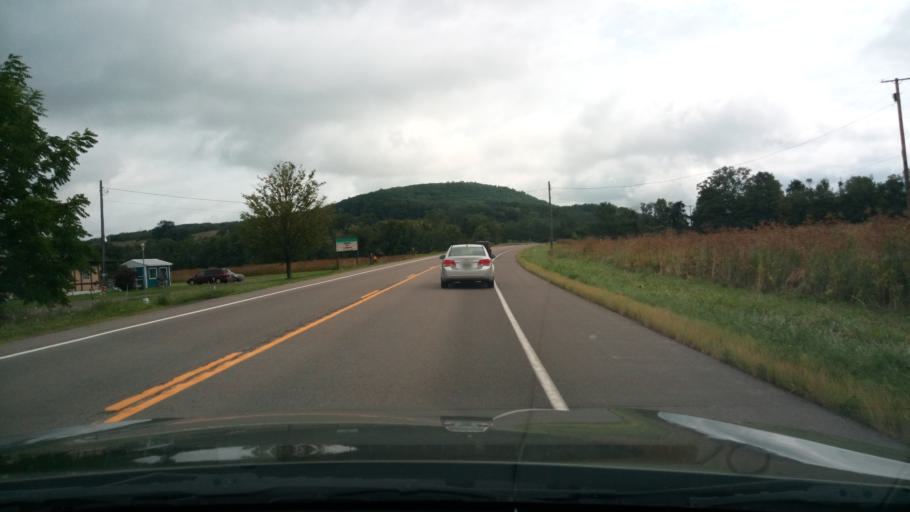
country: US
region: New York
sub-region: Schuyler County
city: Montour Falls
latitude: 42.3216
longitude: -76.6604
